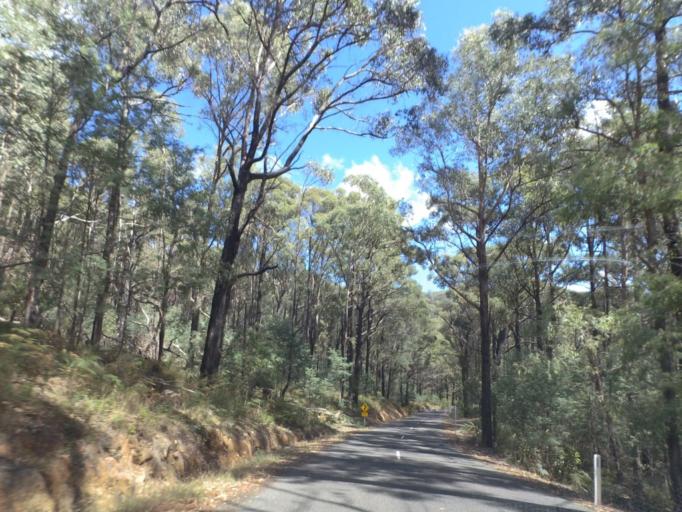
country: AU
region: Victoria
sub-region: Murrindindi
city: Alexandra
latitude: -37.3351
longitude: 145.9488
